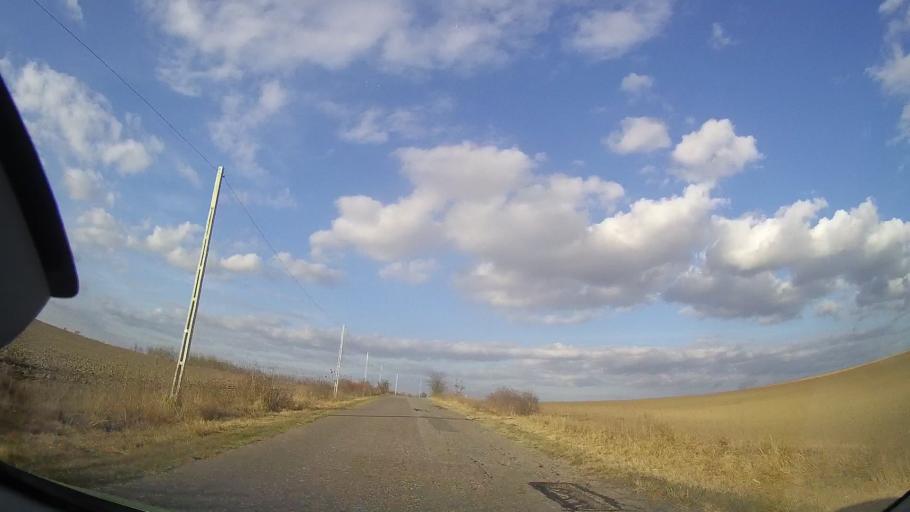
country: RO
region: Constanta
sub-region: Comuna Cerchezu
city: Cerchezu
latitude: 43.8446
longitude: 28.0985
